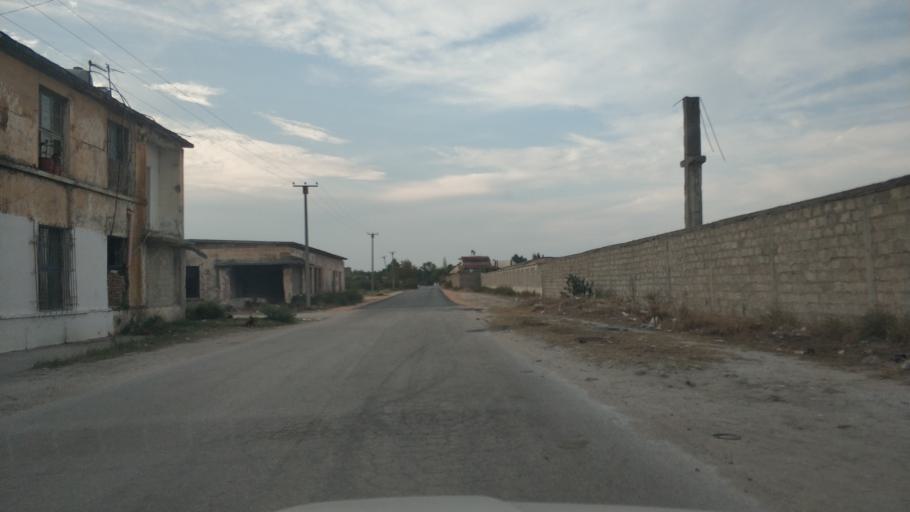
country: AL
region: Vlore
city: Vlore
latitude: 40.4744
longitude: 19.4554
